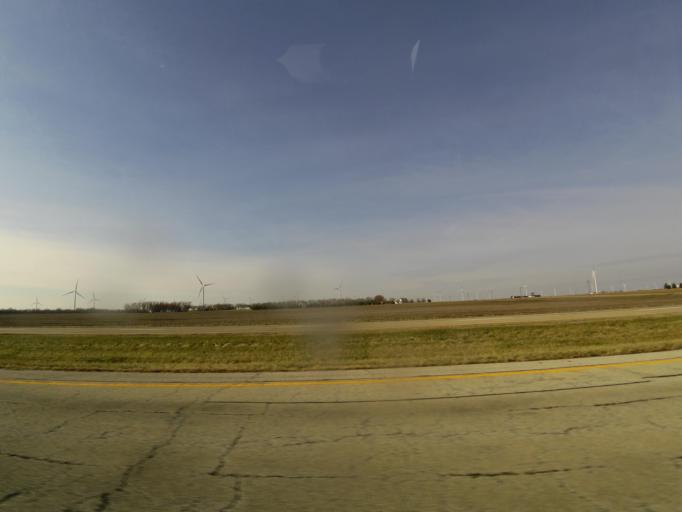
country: US
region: Illinois
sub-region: Macon County
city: Maroa
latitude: 39.9921
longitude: -88.9561
